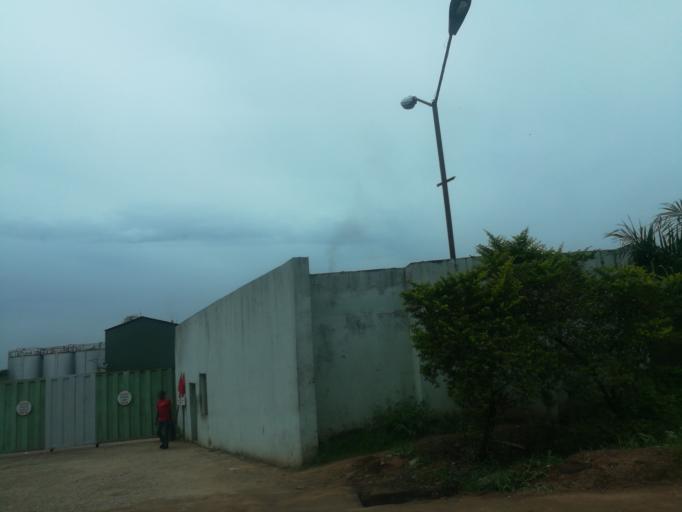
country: NG
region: Oyo
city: Ibadan
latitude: 7.3327
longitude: 3.8925
